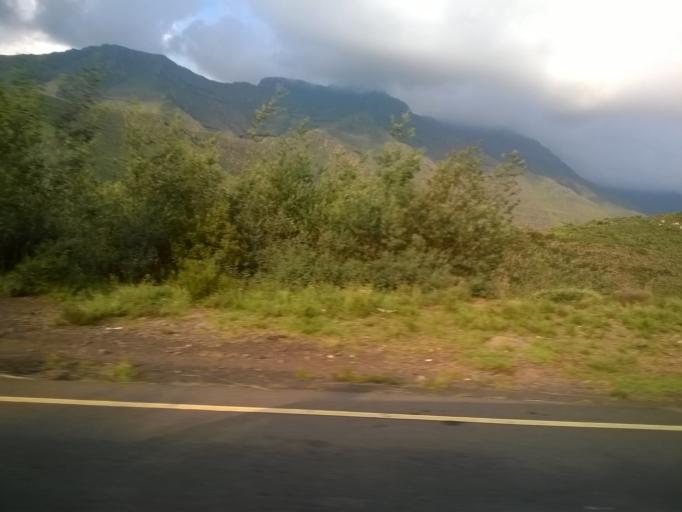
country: LS
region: Butha-Buthe
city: Butha-Buthe
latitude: -29.0588
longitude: 28.3556
